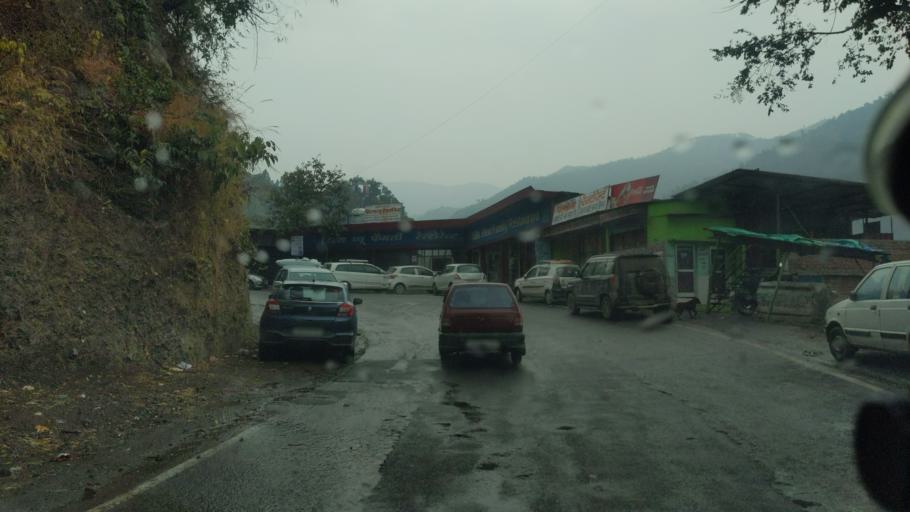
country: IN
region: Uttarakhand
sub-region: Naini Tal
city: Bhim Tal
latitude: 29.3024
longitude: 79.5591
